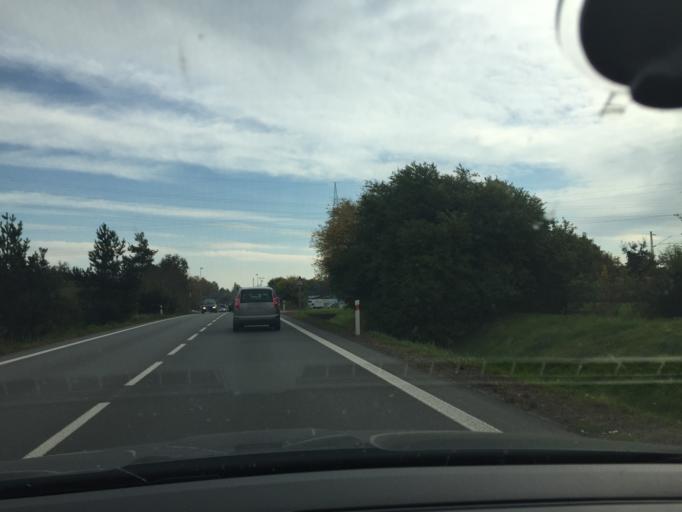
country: CZ
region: Praha
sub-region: Praha 14
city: Hostavice
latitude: 50.0901
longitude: 14.5445
